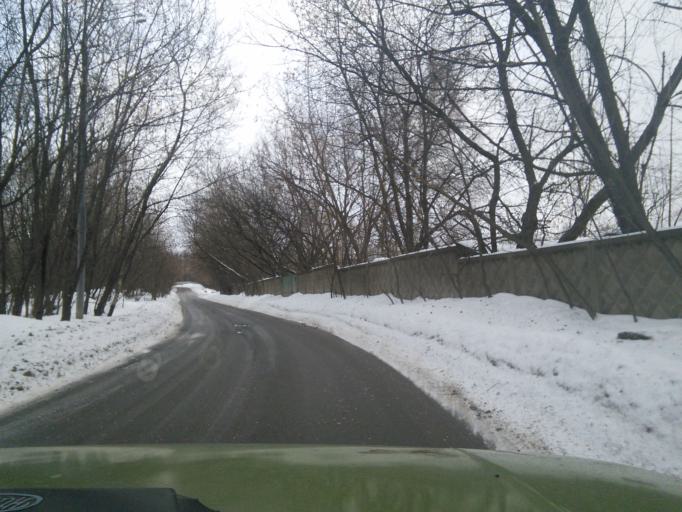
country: RU
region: Moskovskaya
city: Fili
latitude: 55.7572
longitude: 37.4728
